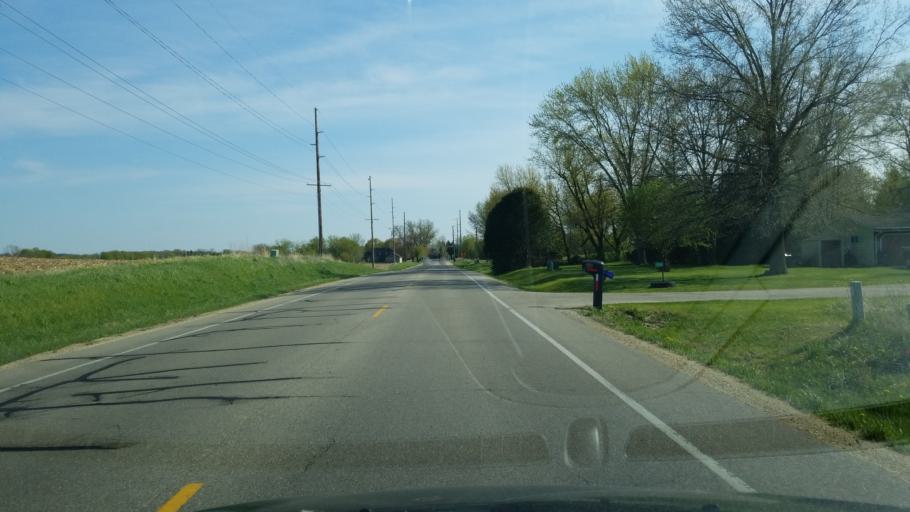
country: US
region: Wisconsin
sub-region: Dane County
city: Fitchburg
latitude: 42.9335
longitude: -89.4379
